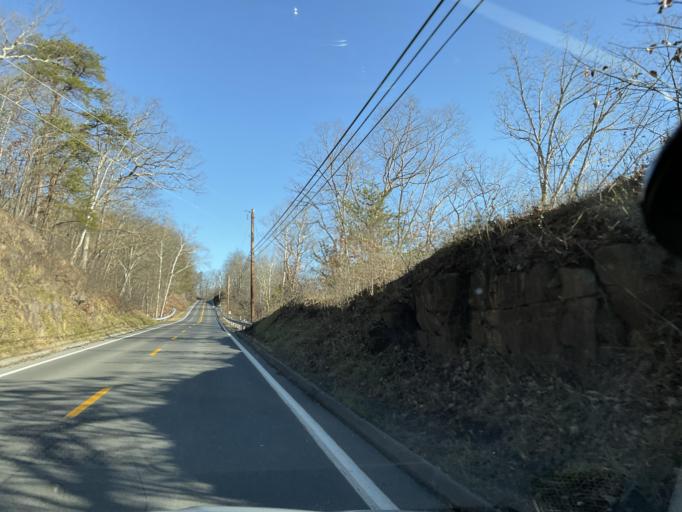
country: US
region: West Virginia
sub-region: Mineral County
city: Fort Ashby
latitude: 39.5267
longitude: -78.5245
